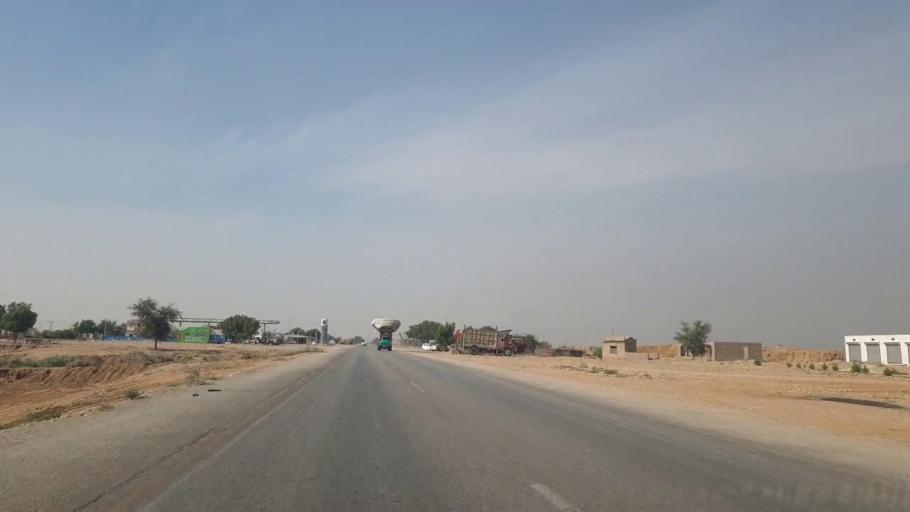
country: PK
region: Sindh
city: Sann
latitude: 26.0266
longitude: 68.1272
